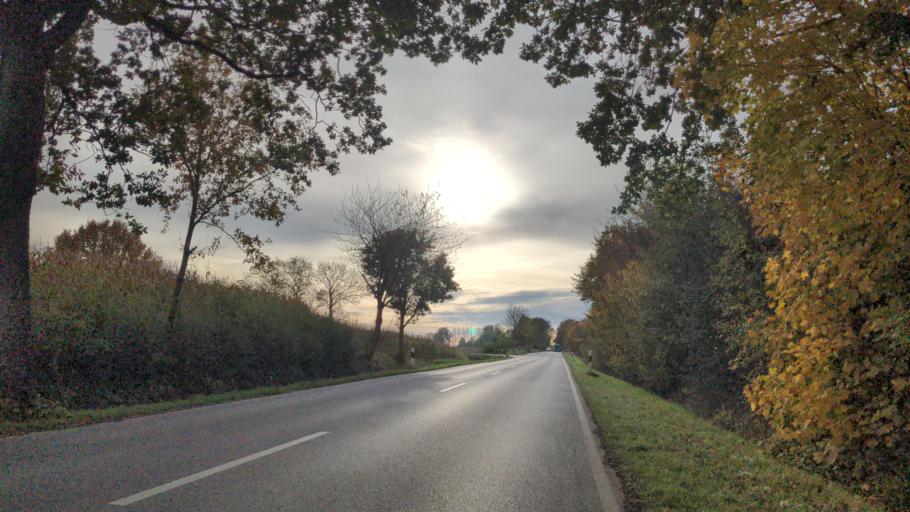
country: DE
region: Schleswig-Holstein
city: Glasau
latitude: 54.1074
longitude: 10.5374
